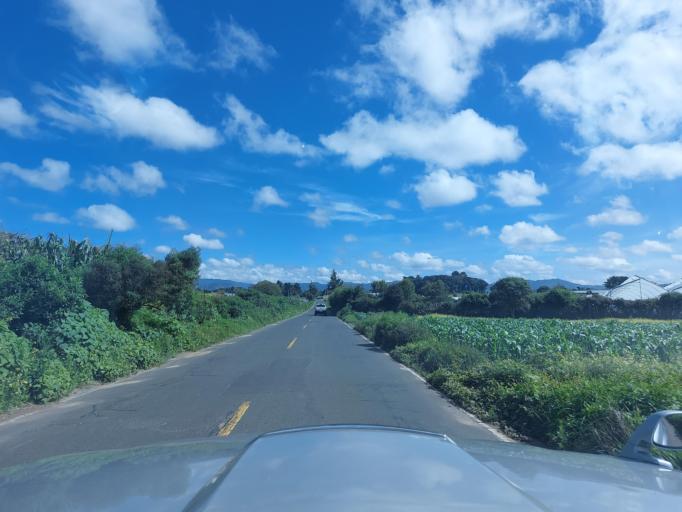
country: GT
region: Chimaltenango
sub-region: Municipio de Zaragoza
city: Zaragoza
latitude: 14.6616
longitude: -90.8983
